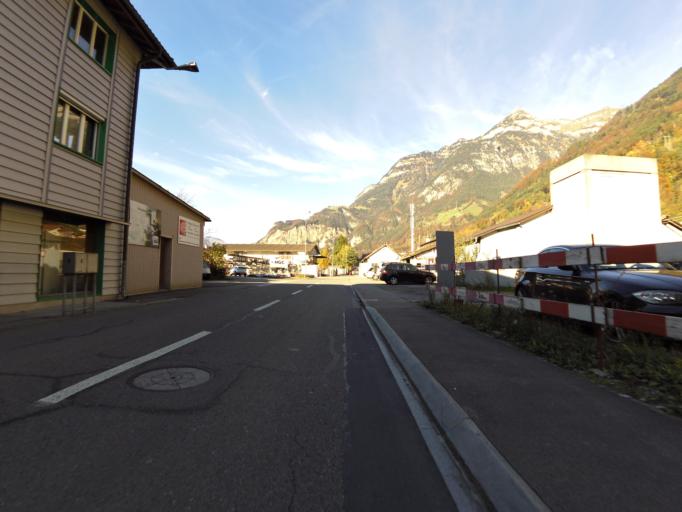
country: CH
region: Uri
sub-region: Uri
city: Flueelen
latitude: 46.8998
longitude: 8.6238
